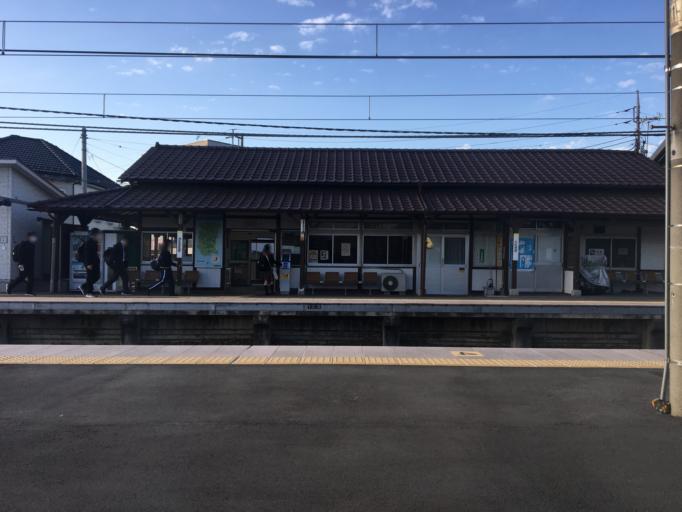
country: JP
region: Gunma
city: Isesaki
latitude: 36.3586
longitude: 139.2419
